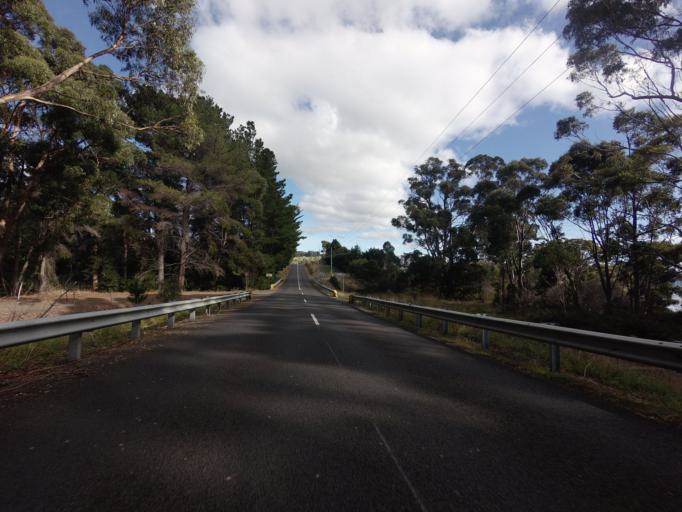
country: AU
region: Tasmania
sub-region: Clarence
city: Sandford
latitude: -43.0534
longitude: 147.7839
